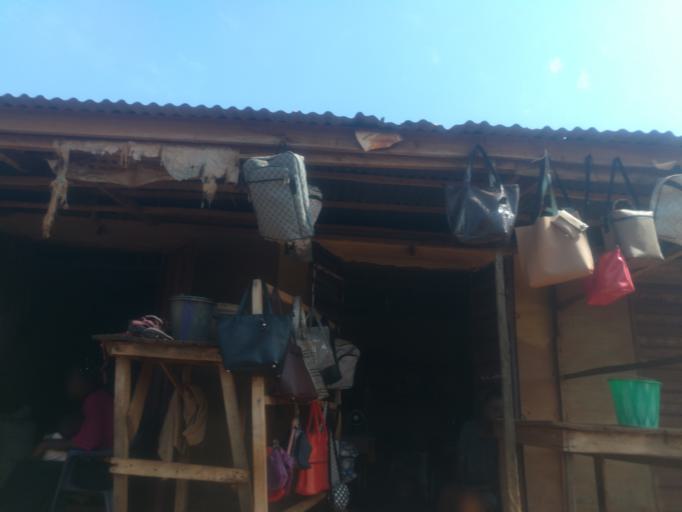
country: NG
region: Oyo
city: Egbeda
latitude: 7.4151
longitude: 3.9922
